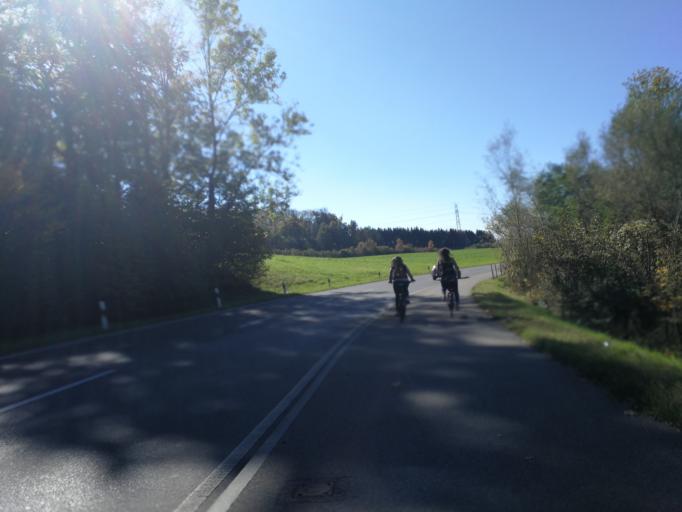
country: CH
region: Zurich
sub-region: Bezirk Hinwil
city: Binzikon
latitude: 47.2911
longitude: 8.7751
